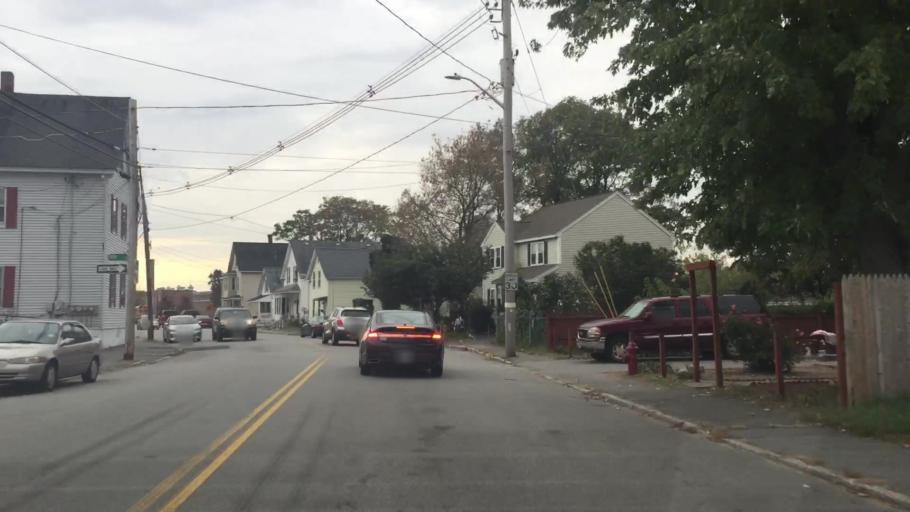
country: US
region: Massachusetts
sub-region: Middlesex County
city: Dracut
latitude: 42.6546
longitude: -71.3120
